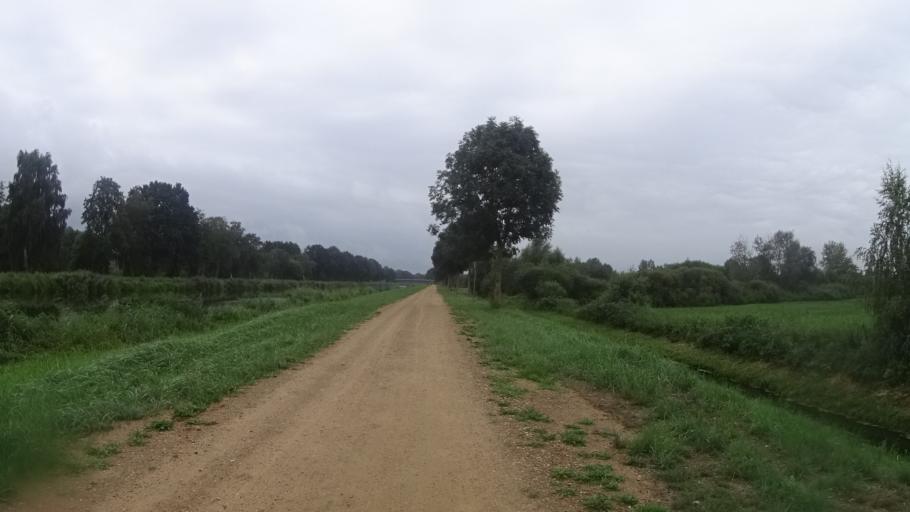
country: DE
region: Schleswig-Holstein
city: Buchen
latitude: 53.4859
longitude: 10.6304
